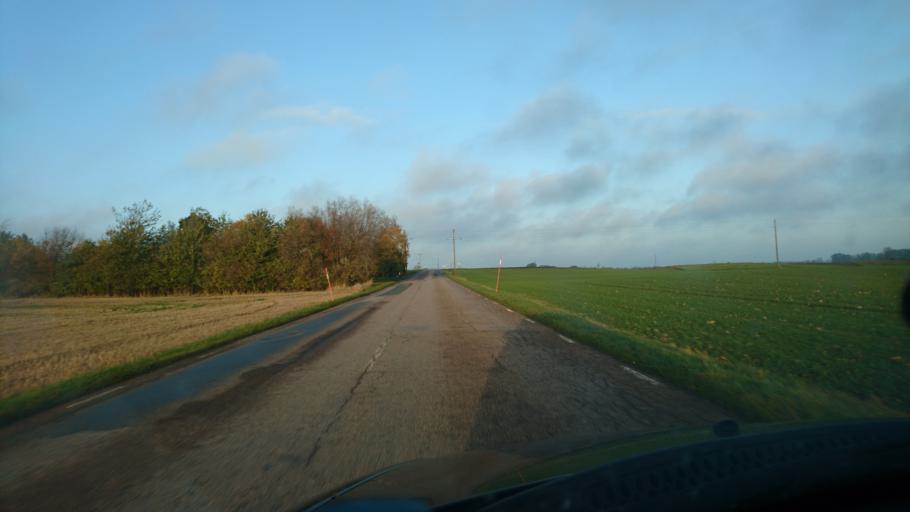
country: SE
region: Skane
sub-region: Tomelilla Kommun
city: Tomelilla
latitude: 55.4498
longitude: 14.1453
